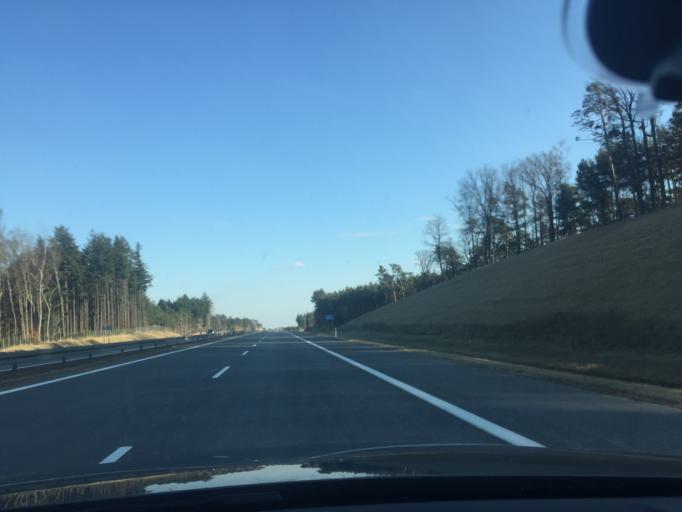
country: PL
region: Lubusz
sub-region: Powiat miedzyrzecki
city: Brojce
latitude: 52.3105
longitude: 15.6147
